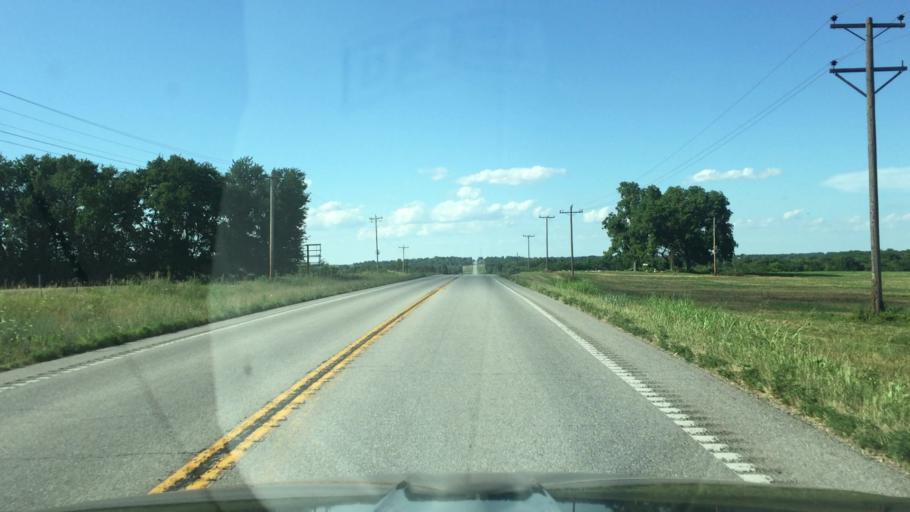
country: US
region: Missouri
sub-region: Morgan County
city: Versailles
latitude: 38.5362
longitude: -92.7981
